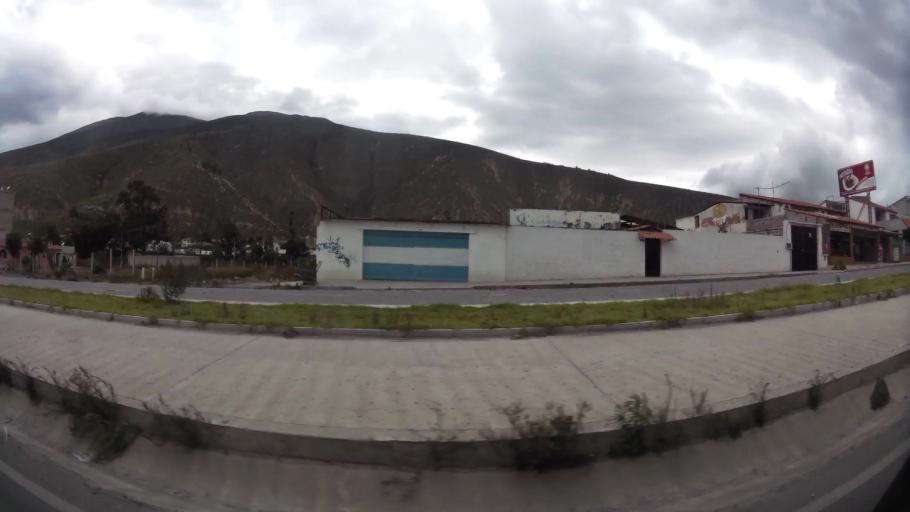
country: EC
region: Pichincha
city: Quito
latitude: -0.0112
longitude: -78.4529
